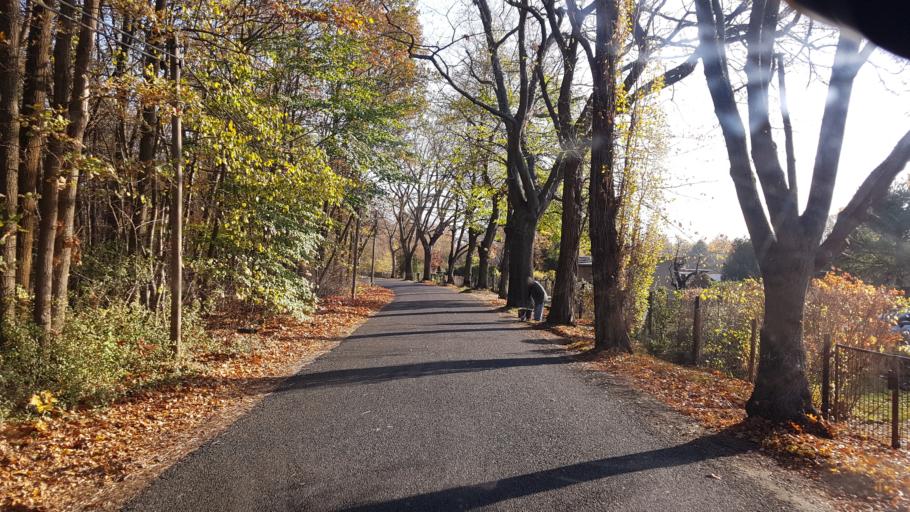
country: DE
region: Brandenburg
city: Schipkau
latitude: 51.5606
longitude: 13.9127
